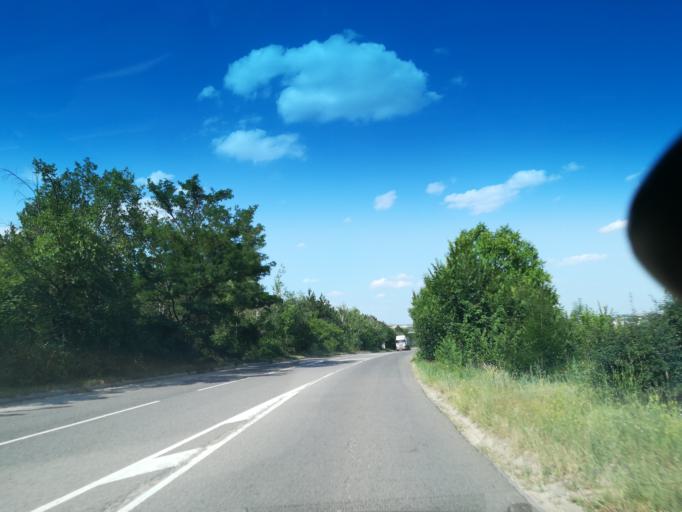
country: BG
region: Stara Zagora
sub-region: Obshtina Chirpan
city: Chirpan
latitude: 42.2282
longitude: 25.3931
